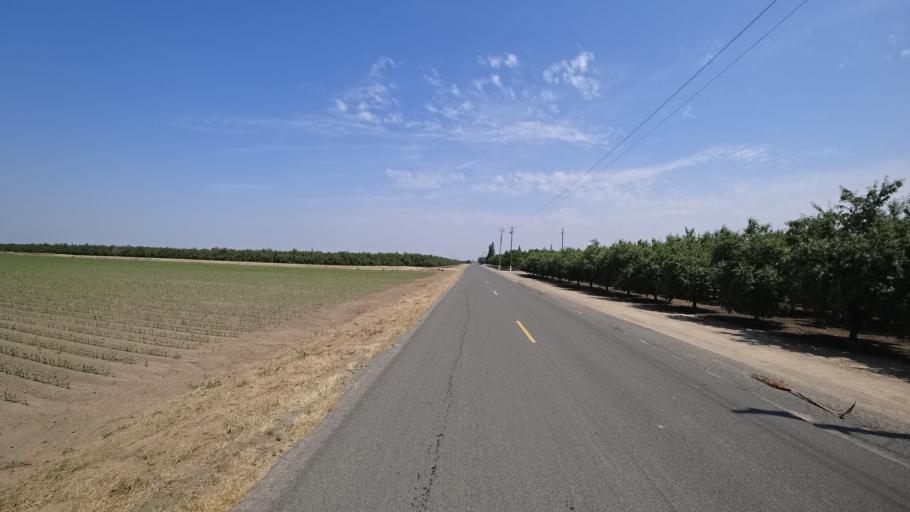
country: US
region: California
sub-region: Kings County
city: Armona
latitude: 36.3200
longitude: -119.7449
